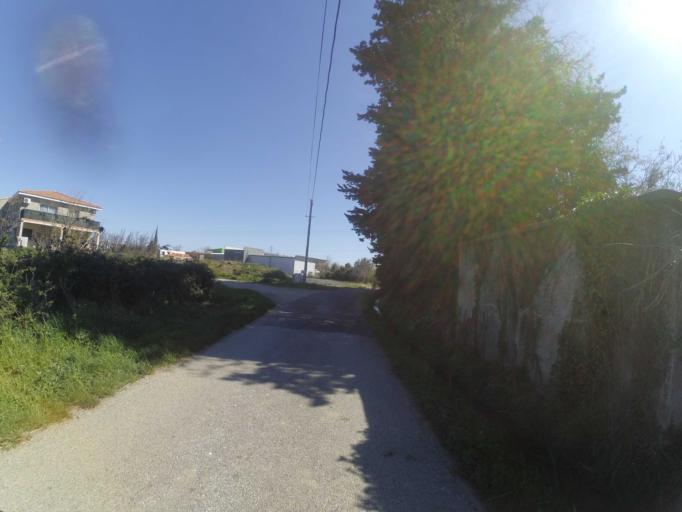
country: FR
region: Languedoc-Roussillon
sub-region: Departement des Pyrenees-Orientales
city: Millas
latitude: 42.6859
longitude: 2.7056
